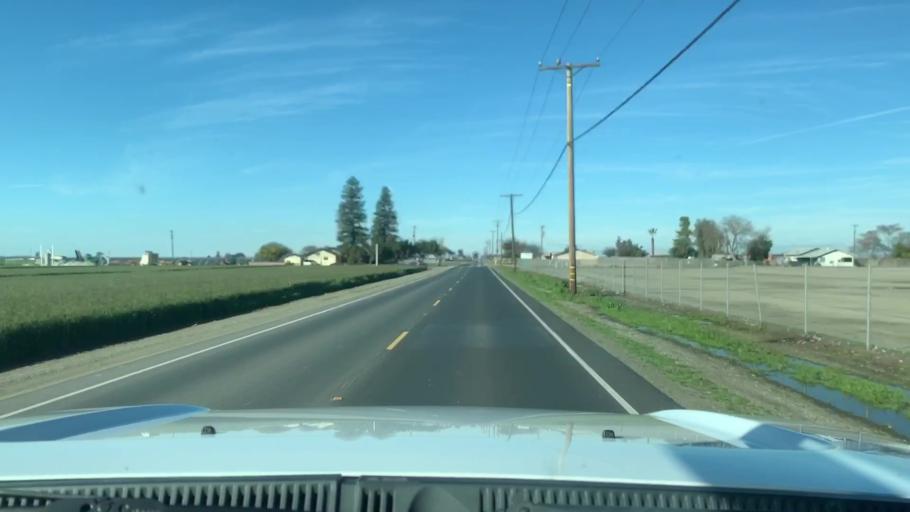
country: US
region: California
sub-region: Kings County
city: Corcoran
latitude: 36.1866
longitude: -119.4933
